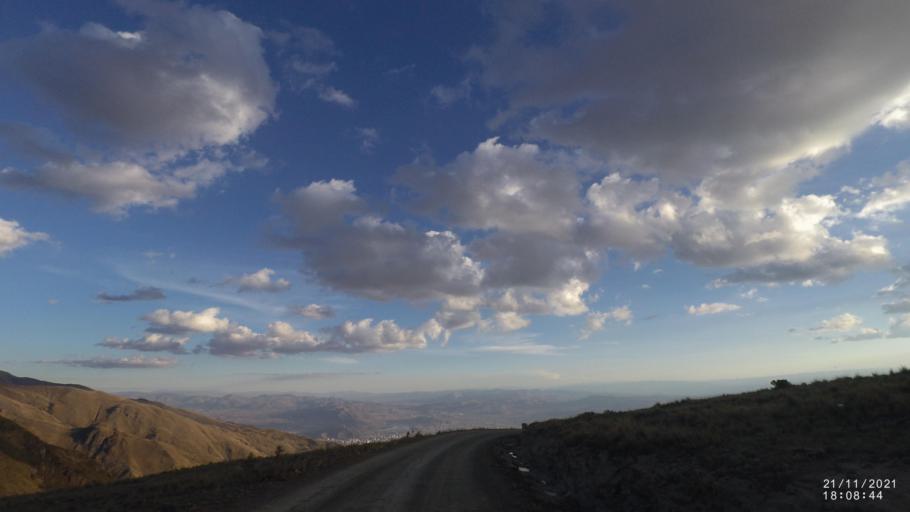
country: BO
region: Cochabamba
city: Cochabamba
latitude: -17.2812
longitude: -66.2096
